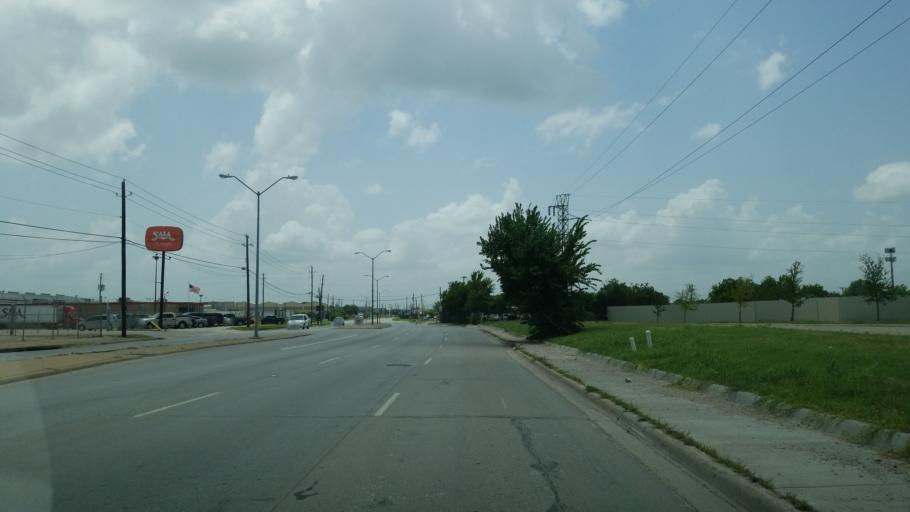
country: US
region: Texas
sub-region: Dallas County
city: Cockrell Hill
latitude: 32.7790
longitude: -96.8898
